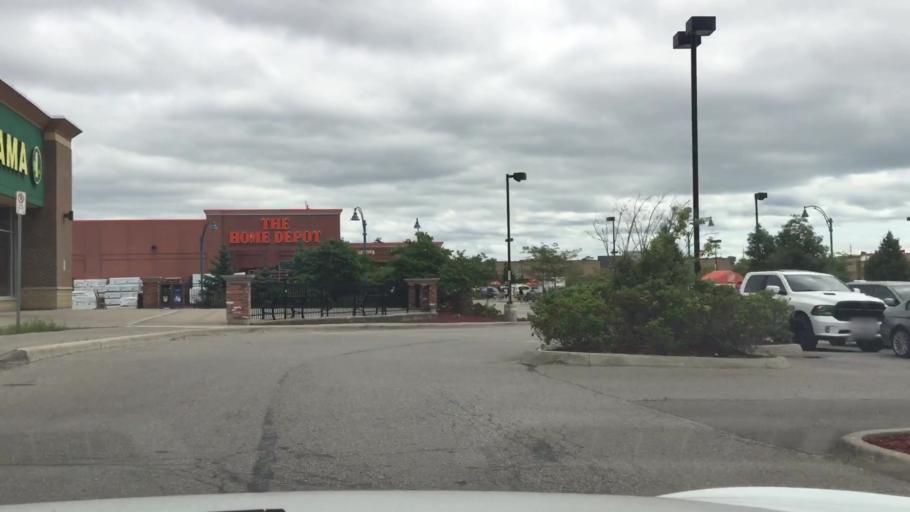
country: CA
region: Ontario
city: Oshawa
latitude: 43.9106
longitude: -78.7112
